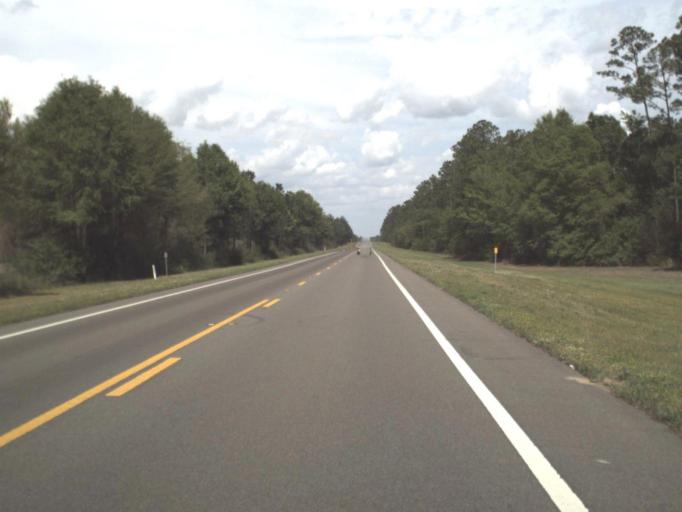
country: US
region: Florida
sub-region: Santa Rosa County
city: East Milton
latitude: 30.6884
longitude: -86.8202
